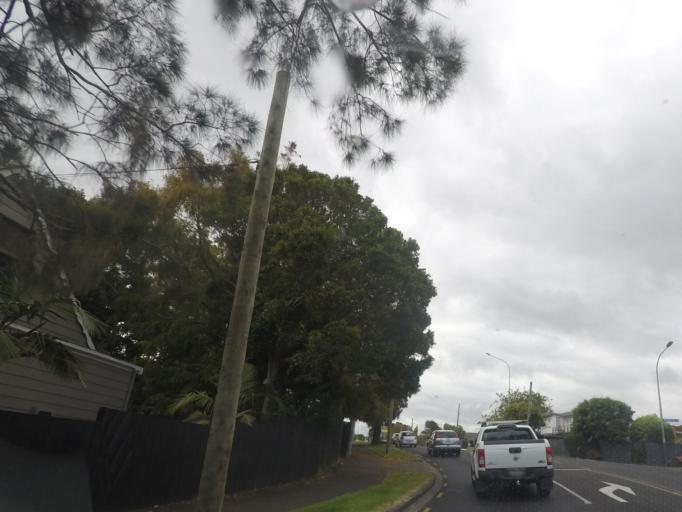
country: NZ
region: Auckland
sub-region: Auckland
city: Tamaki
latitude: -36.8643
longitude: 174.8420
